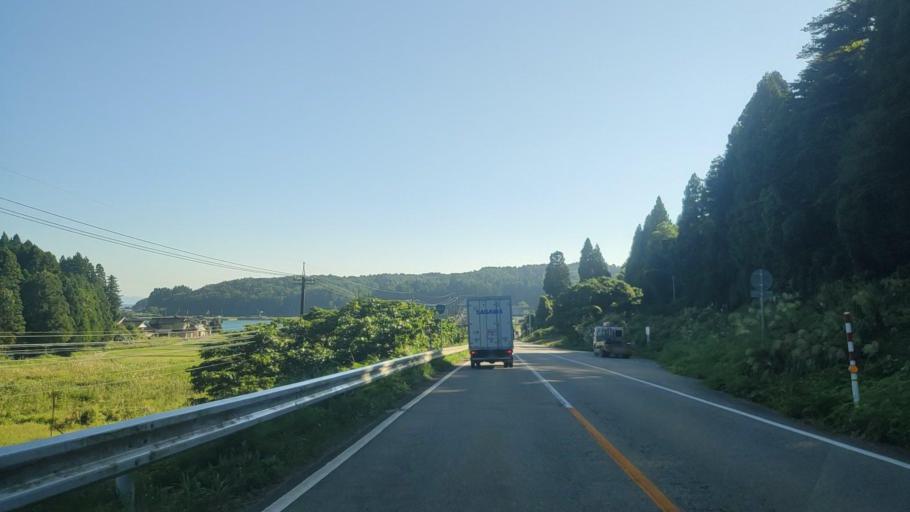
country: JP
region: Ishikawa
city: Nanao
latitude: 37.2069
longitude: 136.9084
